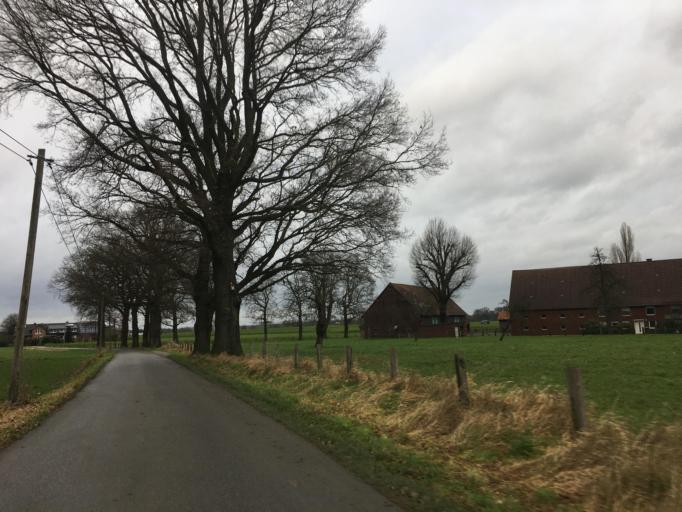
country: DE
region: North Rhine-Westphalia
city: Oer-Erkenschwick
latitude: 51.6801
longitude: 7.3106
